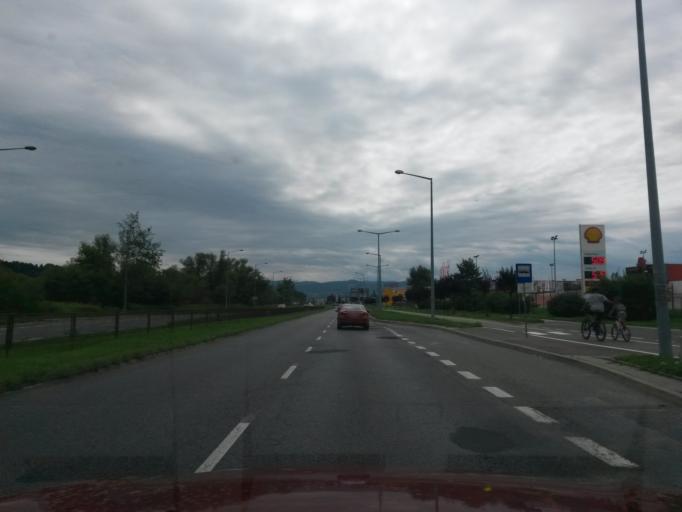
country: PL
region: Lesser Poland Voivodeship
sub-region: Powiat nowosadecki
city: Nowy Sacz
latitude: 49.6056
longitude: 20.7286
